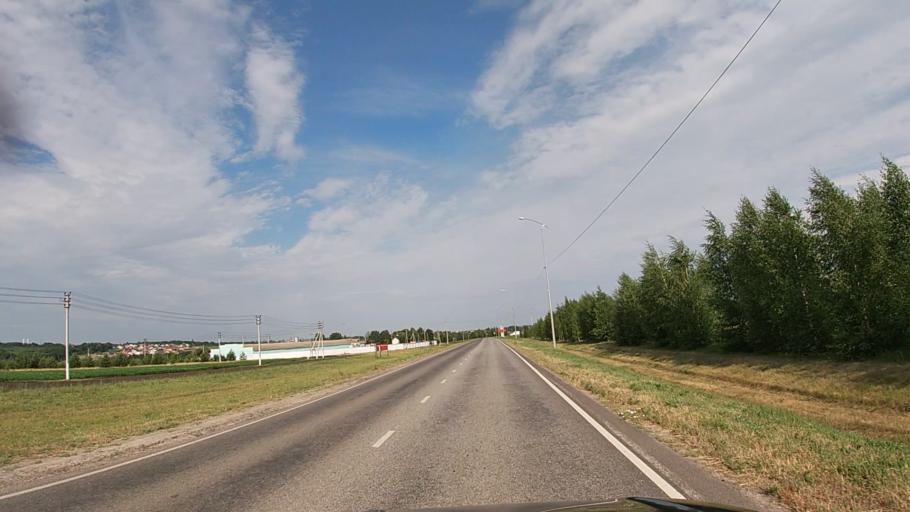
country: RU
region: Belgorod
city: Krasnaya Yaruga
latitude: 50.7980
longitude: 35.6838
